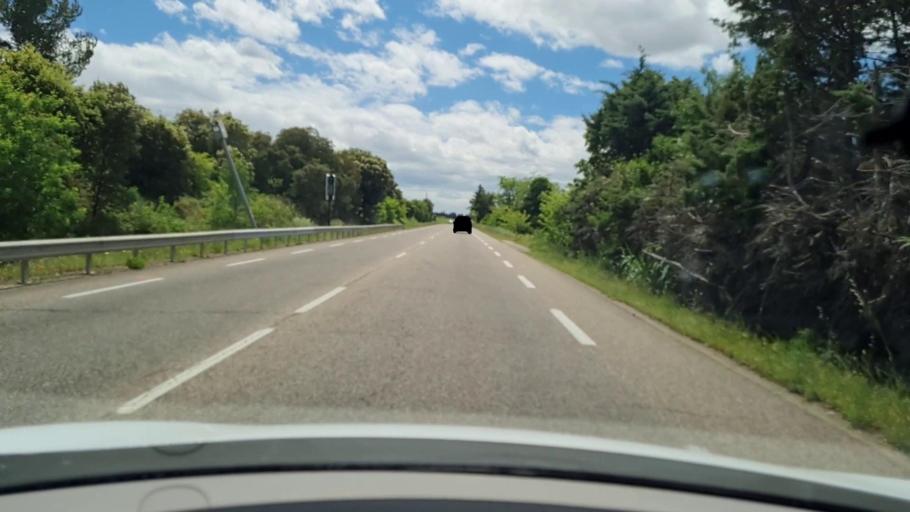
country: FR
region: Languedoc-Roussillon
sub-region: Departement du Gard
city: Aubord
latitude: 43.7463
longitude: 4.3010
